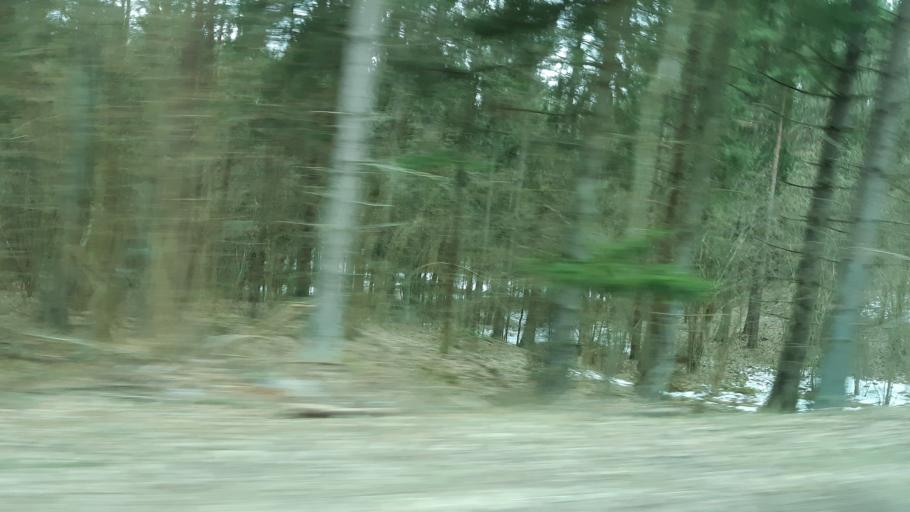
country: PL
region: Podlasie
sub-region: Suwalki
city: Suwalki
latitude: 54.2857
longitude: 22.9522
